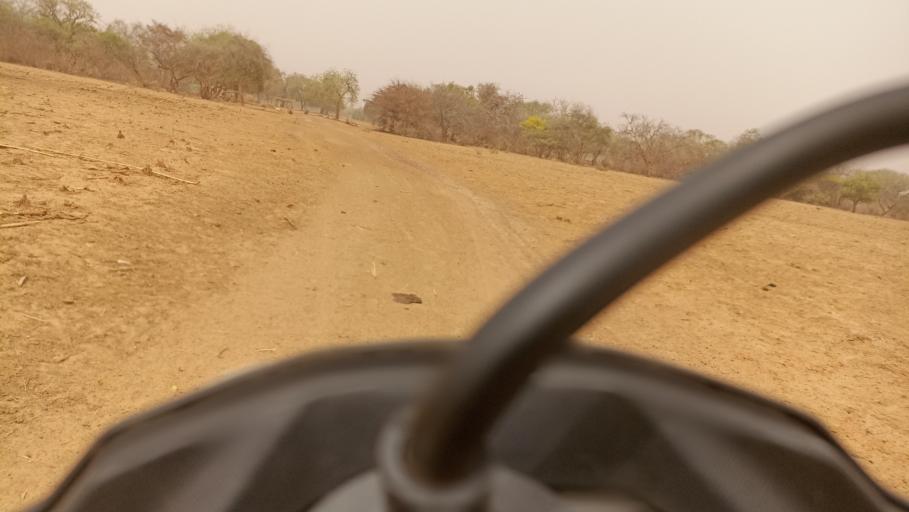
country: BF
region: Nord
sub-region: Province du Zondoma
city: Gourcy
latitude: 13.2498
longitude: -2.6009
